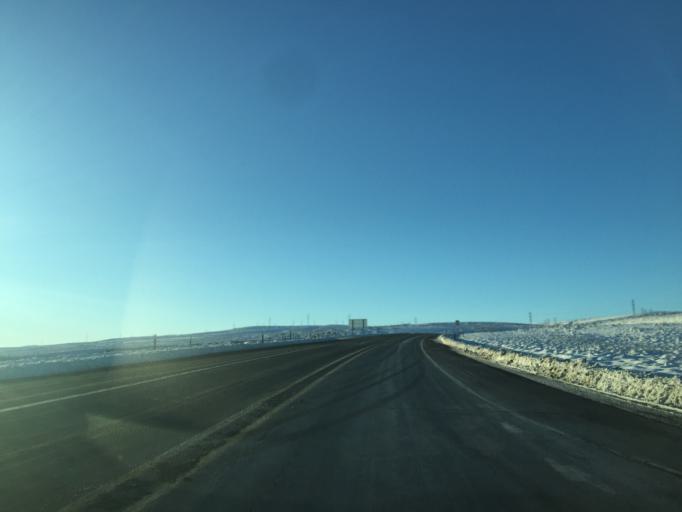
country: US
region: Washington
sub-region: Grant County
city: Soap Lake
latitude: 47.6195
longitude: -119.3648
